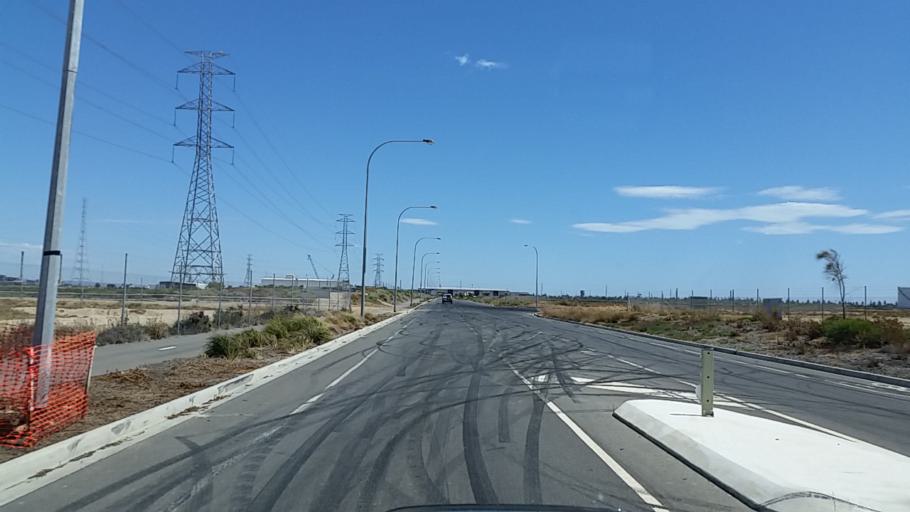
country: AU
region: South Australia
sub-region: Port Adelaide Enfield
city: Birkenhead
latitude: -34.7707
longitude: 138.5101
